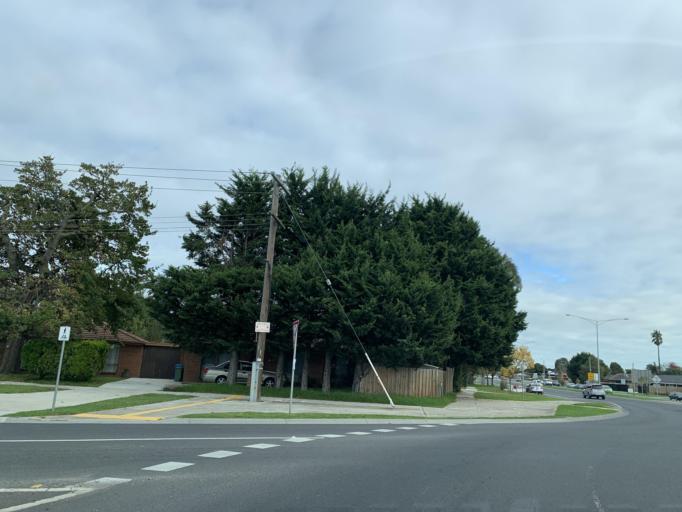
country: AU
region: Victoria
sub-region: Casey
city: Cranbourne
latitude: -38.1142
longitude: 145.2899
